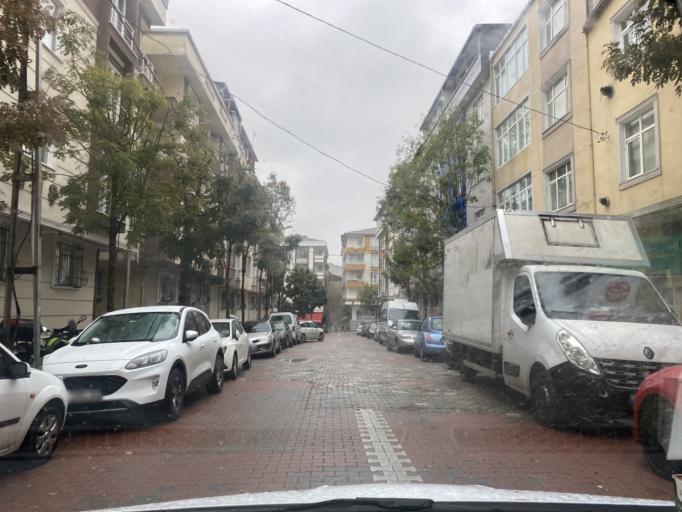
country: TR
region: Istanbul
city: Esenyurt
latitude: 41.0193
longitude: 28.6622
